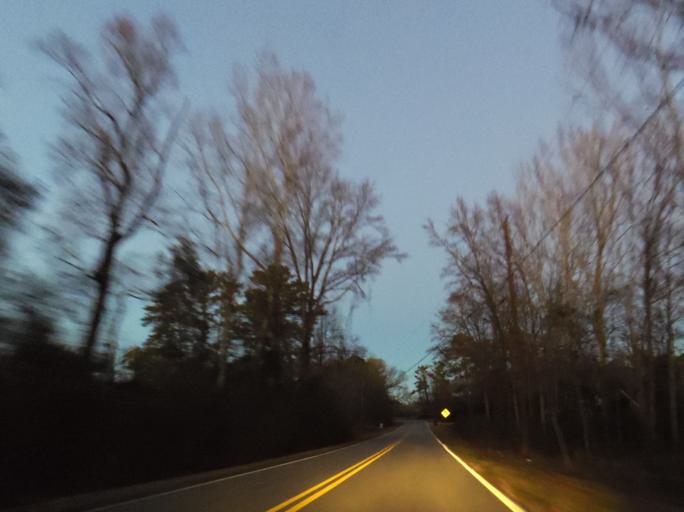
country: US
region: Georgia
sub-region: Peach County
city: Byron
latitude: 32.7236
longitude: -83.7207
